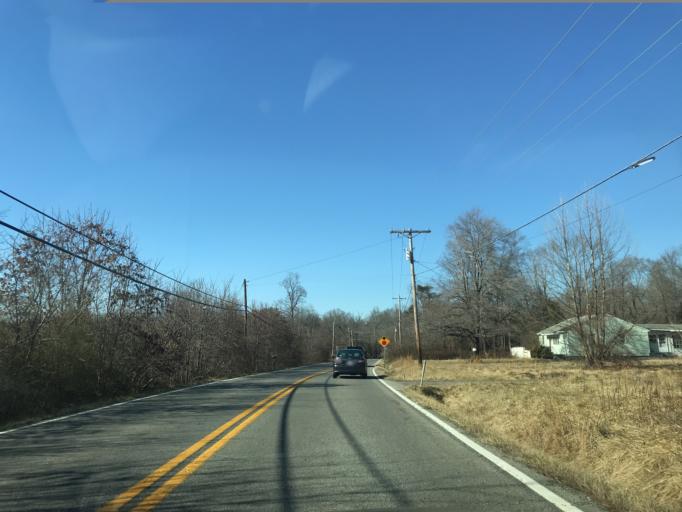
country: US
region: Maryland
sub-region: Charles County
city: Bryans Road
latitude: 38.6065
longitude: -77.0708
